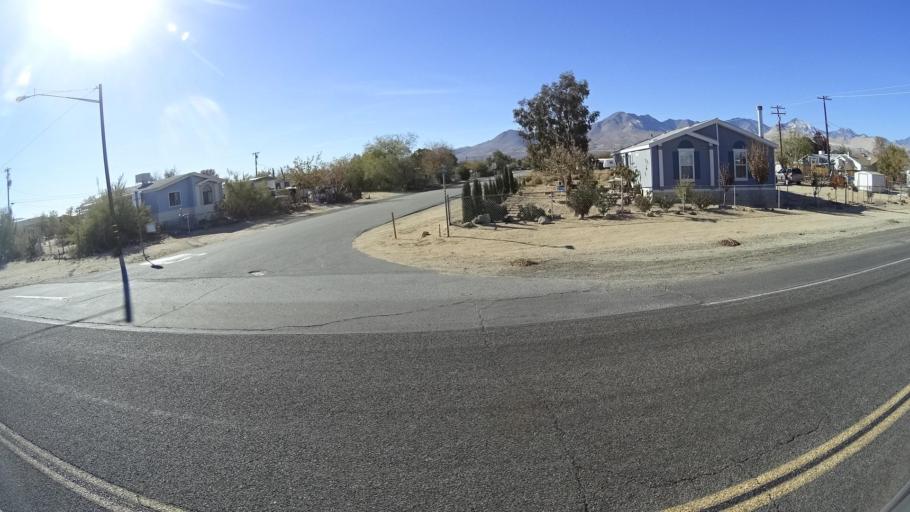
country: US
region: California
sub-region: Kern County
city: Inyokern
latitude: 35.6421
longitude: -117.8110
